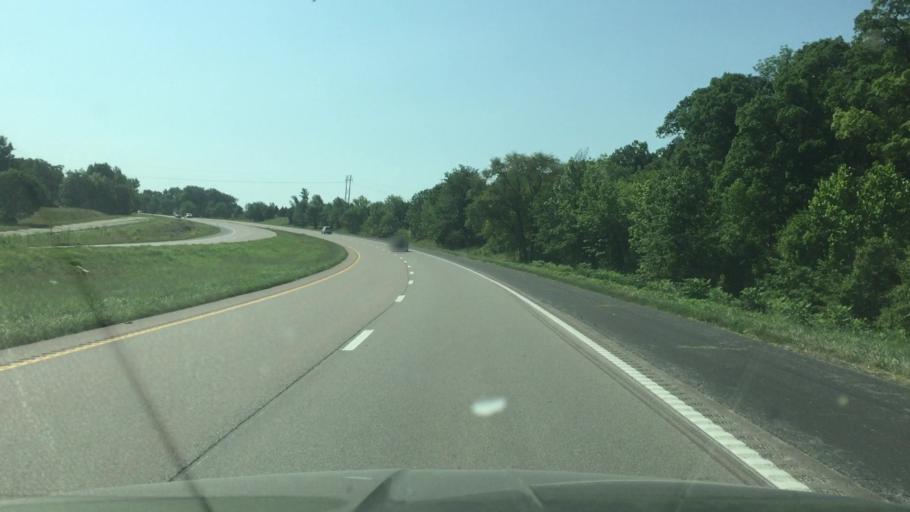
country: US
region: Missouri
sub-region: Pettis County
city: Sedalia
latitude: 38.7222
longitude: -93.3006
